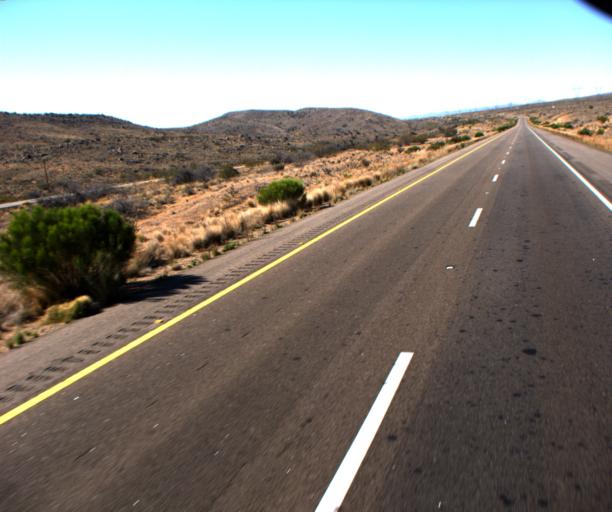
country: US
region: Arizona
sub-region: Mohave County
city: Kingman
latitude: 34.9767
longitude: -113.6693
